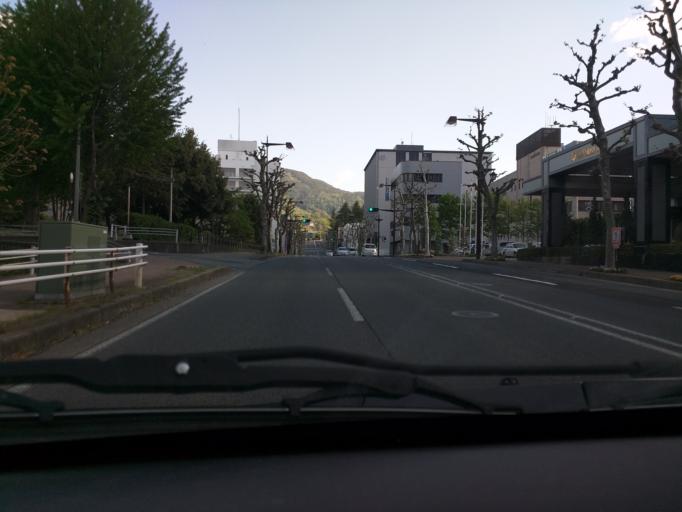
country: JP
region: Nagano
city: Nagano-shi
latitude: 36.6516
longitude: 138.1819
